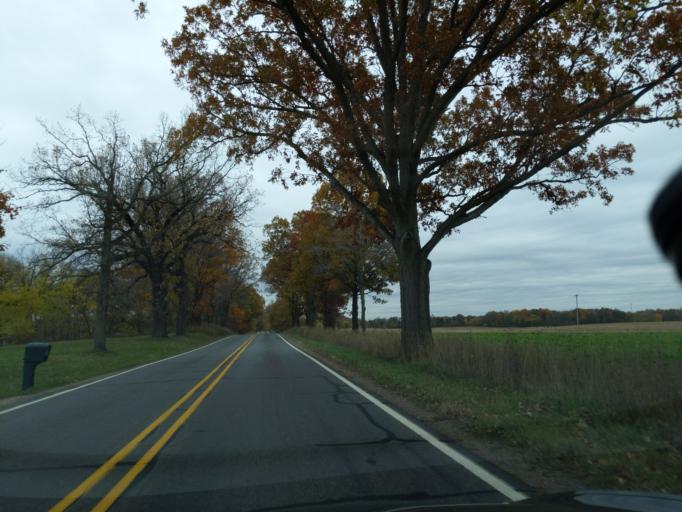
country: US
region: Michigan
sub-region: Jackson County
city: Spring Arbor
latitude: 42.2928
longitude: -84.6002
